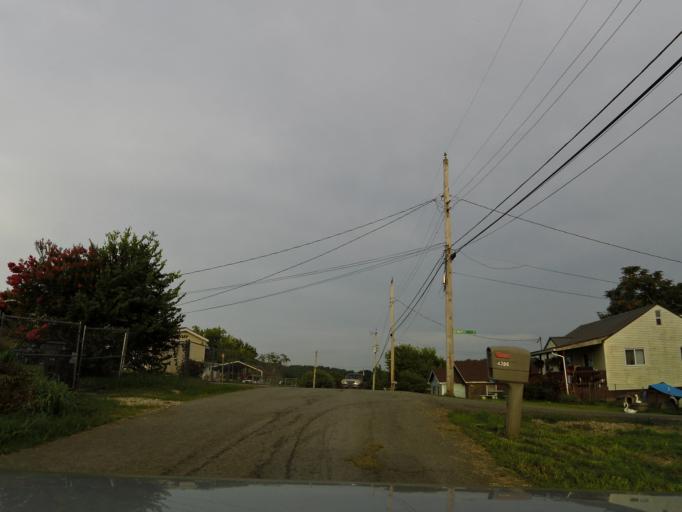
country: US
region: Tennessee
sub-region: Knox County
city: Knoxville
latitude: 35.9307
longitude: -83.9249
